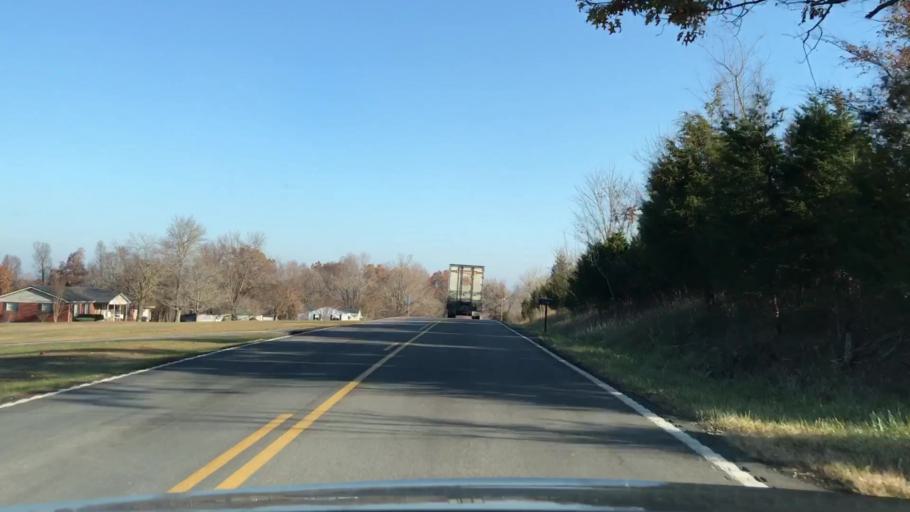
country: US
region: Kentucky
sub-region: Edmonson County
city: Brownsville
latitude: 37.3227
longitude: -86.2677
